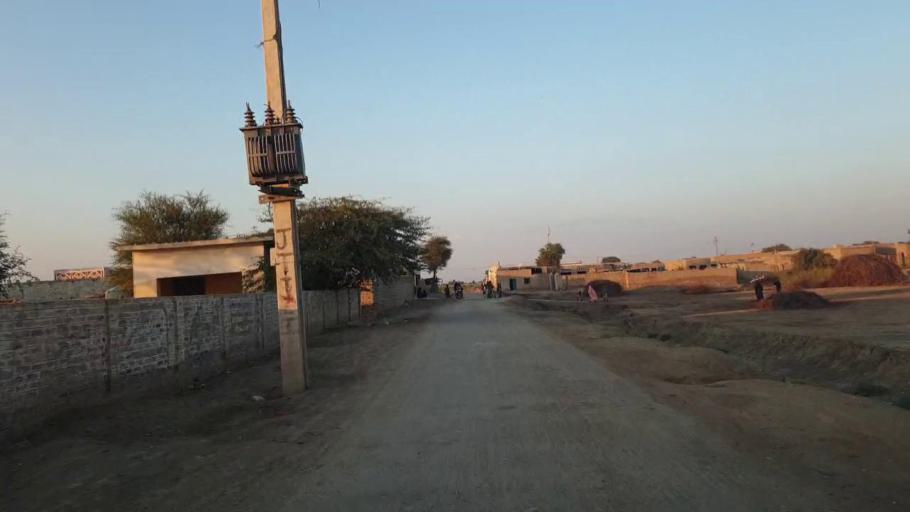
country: PK
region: Sindh
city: Shahpur Chakar
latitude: 26.1595
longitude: 68.5422
